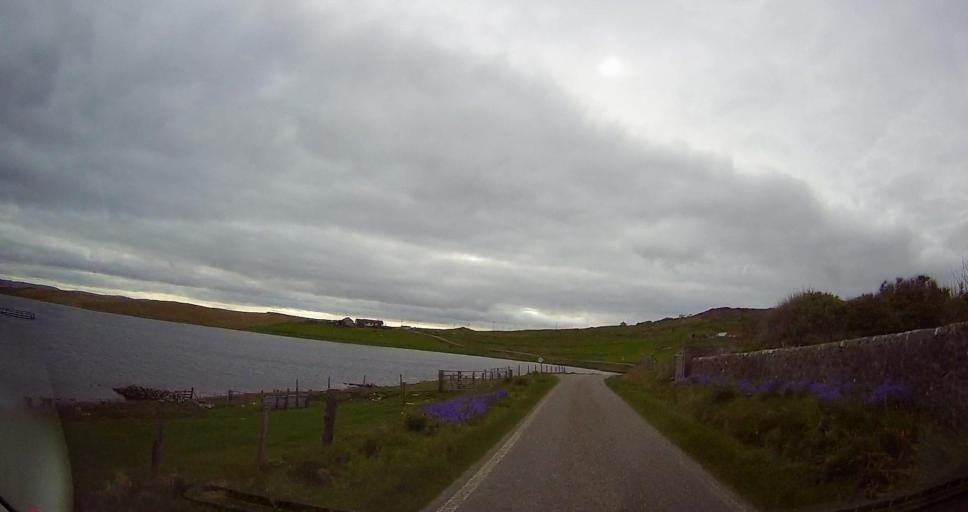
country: GB
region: Scotland
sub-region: Shetland Islands
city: Shetland
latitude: 60.5001
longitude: -1.0701
